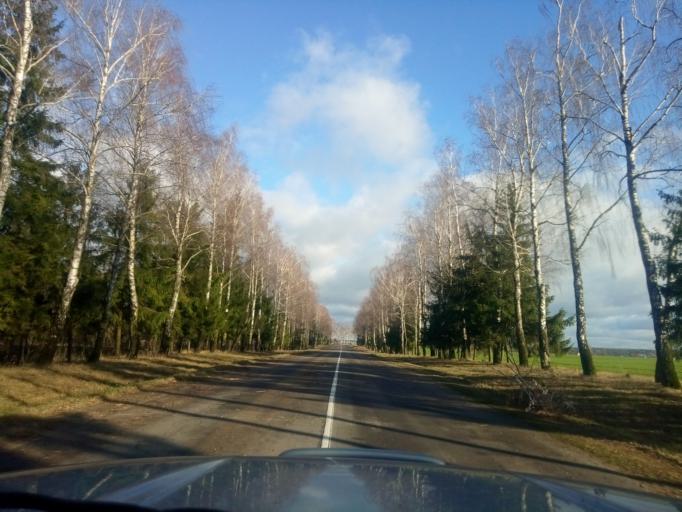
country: BY
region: Minsk
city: Tsimkavichy
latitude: 53.1740
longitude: 26.9387
